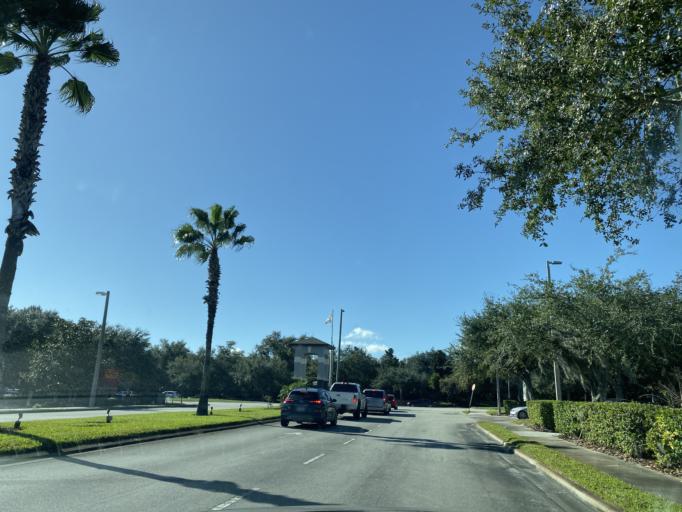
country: US
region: Florida
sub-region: Orange County
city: Taft
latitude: 28.4122
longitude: -81.2421
